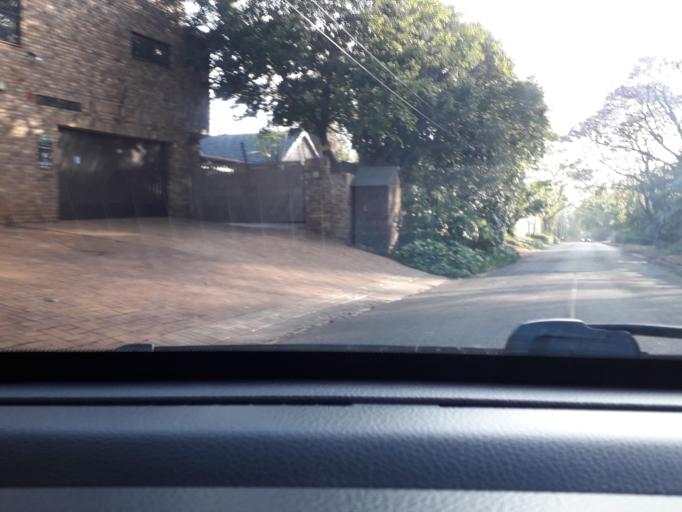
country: ZA
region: Gauteng
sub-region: City of Johannesburg Metropolitan Municipality
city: Johannesburg
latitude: -26.1175
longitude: 28.0632
